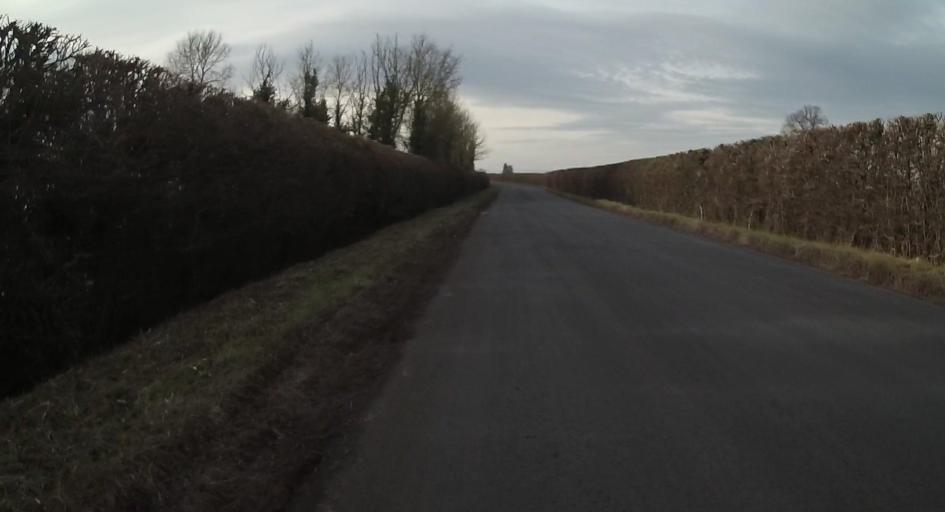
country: GB
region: England
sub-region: West Berkshire
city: Stratfield Mortimer
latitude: 51.4043
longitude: -1.0332
